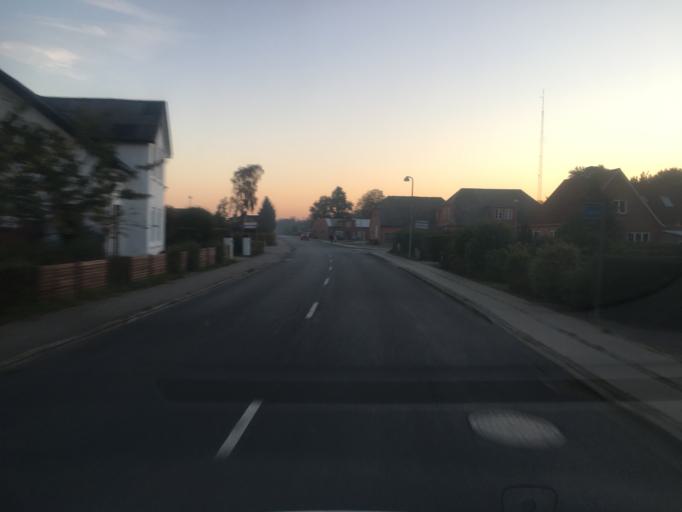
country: DE
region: Schleswig-Holstein
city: Bramstedtlund
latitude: 54.9491
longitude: 9.0980
